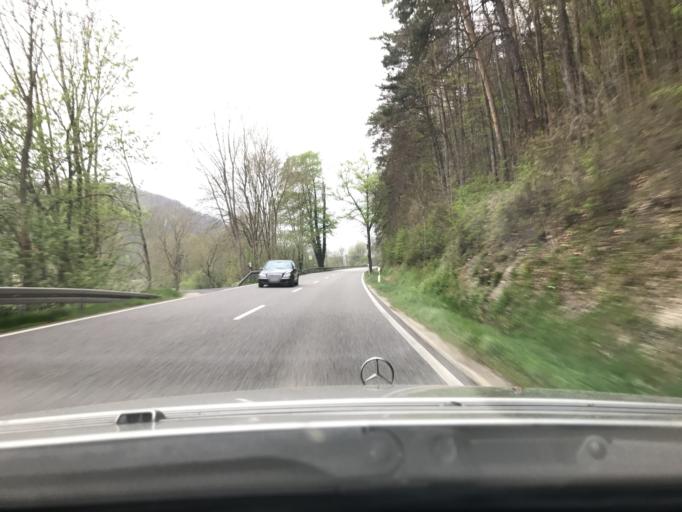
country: DE
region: Thuringia
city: Geisleden
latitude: 51.3551
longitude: 10.1844
